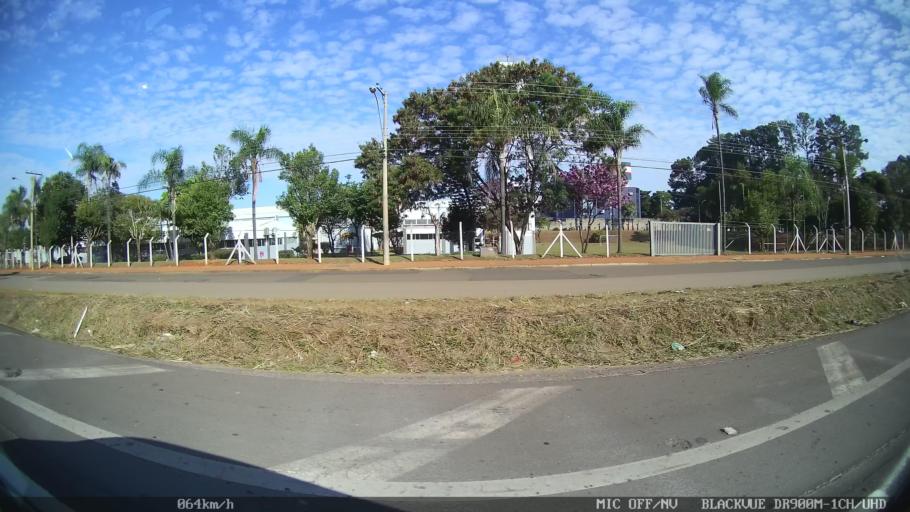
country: BR
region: Sao Paulo
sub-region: Santa Barbara D'Oeste
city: Santa Barbara d'Oeste
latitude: -22.7641
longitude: -47.3821
